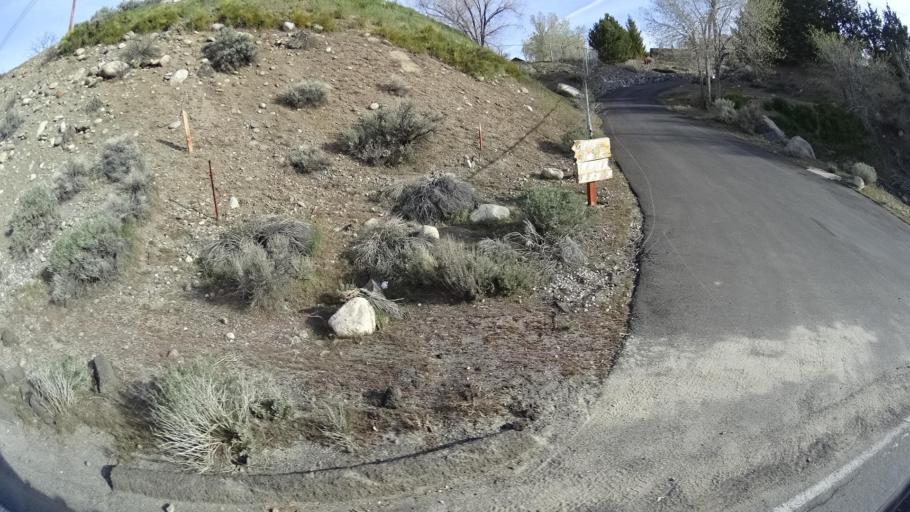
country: US
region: Nevada
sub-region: Washoe County
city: Mogul
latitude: 39.5099
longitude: -119.8977
